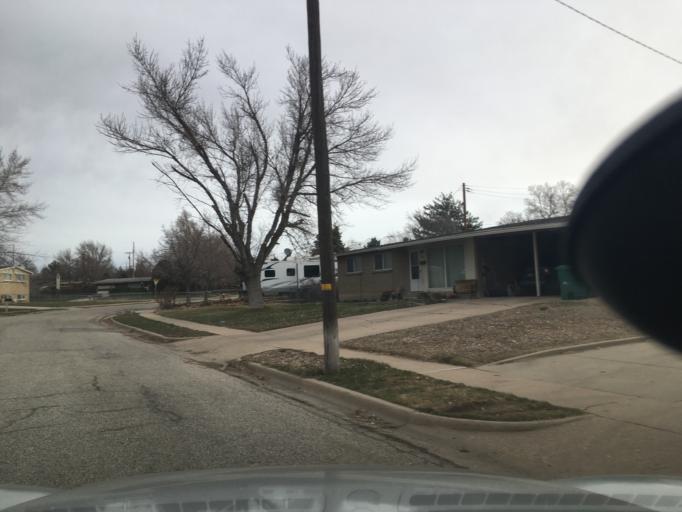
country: US
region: Utah
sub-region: Davis County
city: Layton
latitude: 41.0722
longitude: -111.9682
